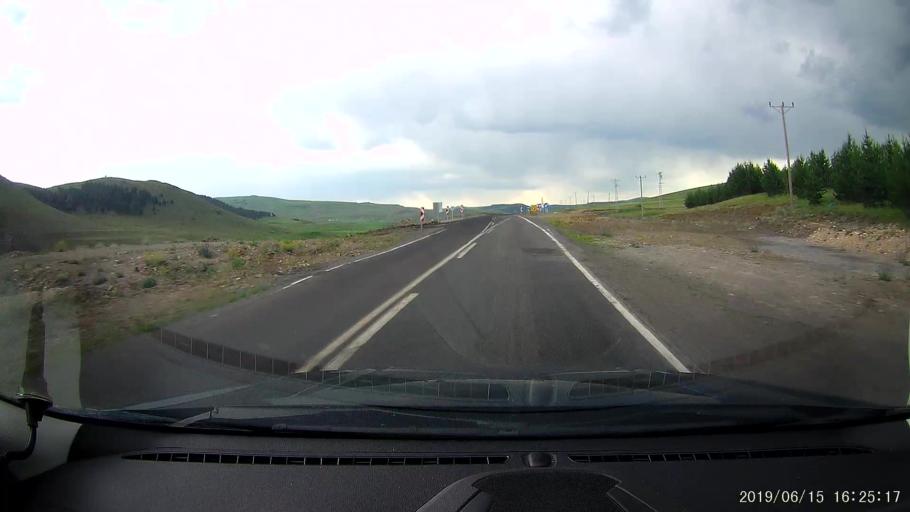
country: TR
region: Ardahan
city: Hanak
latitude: 41.1556
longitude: 42.8707
